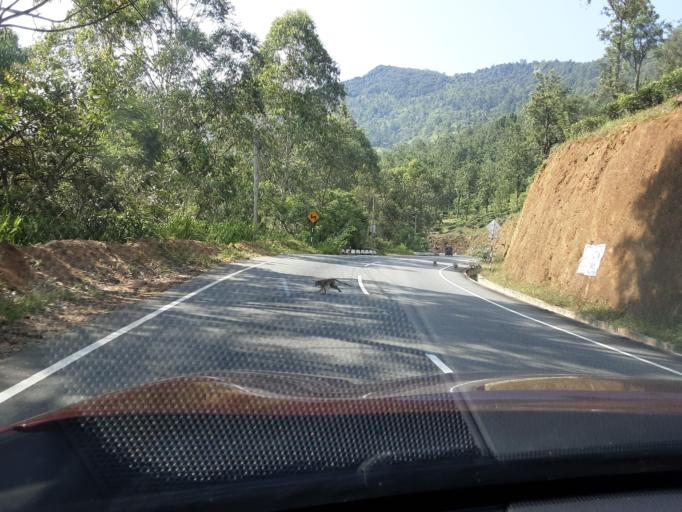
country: LK
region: Uva
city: Badulla
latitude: 6.9630
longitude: 81.0999
